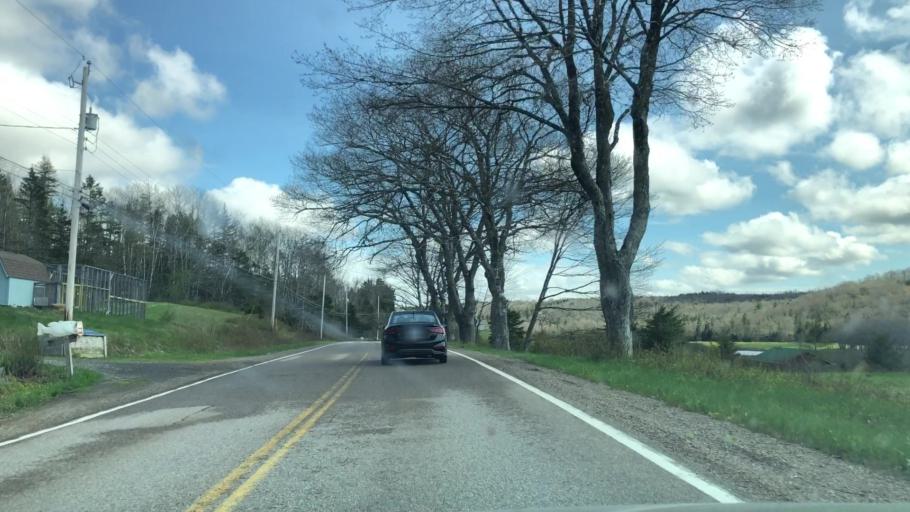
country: CA
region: Nova Scotia
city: Antigonish
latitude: 45.2014
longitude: -62.0034
